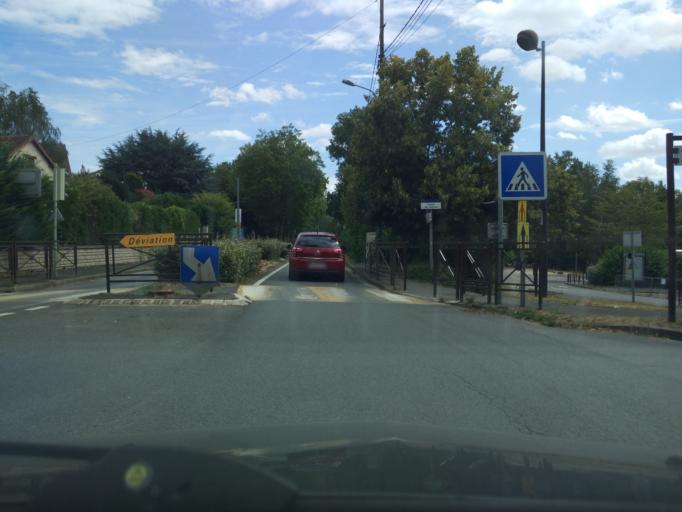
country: FR
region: Ile-de-France
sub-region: Departement de l'Essonne
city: Villiers-le-Bacle
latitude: 48.7048
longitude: 2.1186
